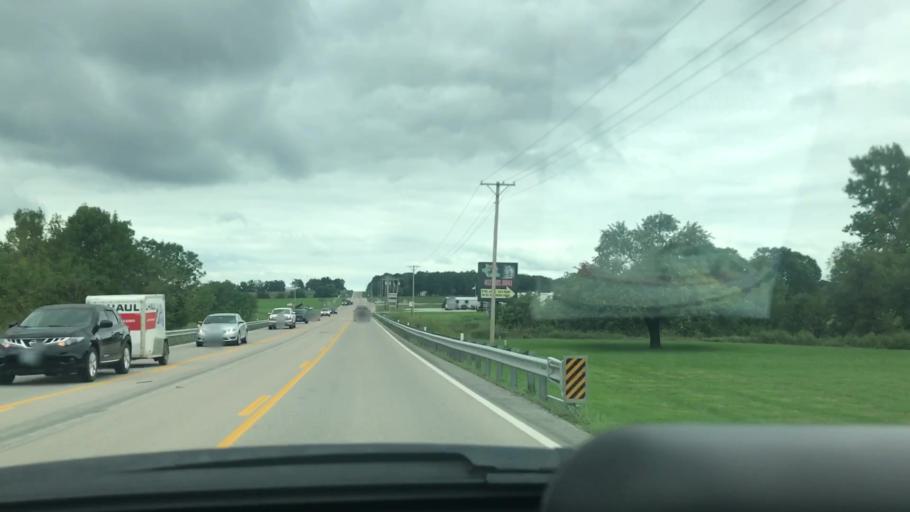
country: US
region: Missouri
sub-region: Dallas County
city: Buffalo
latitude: 37.6636
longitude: -93.1035
